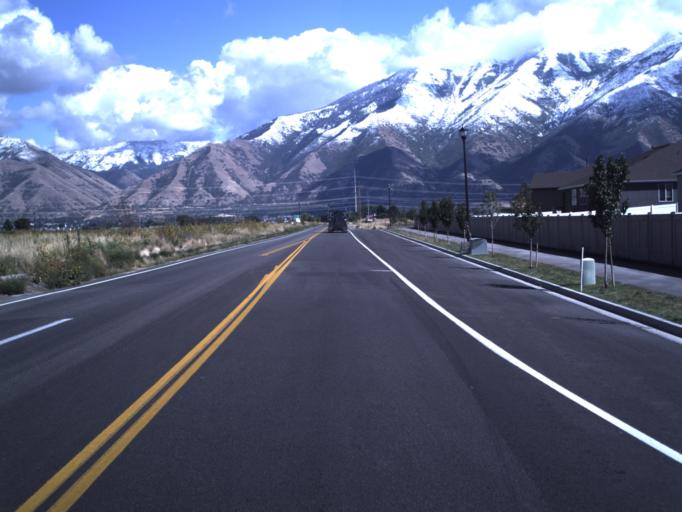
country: US
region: Utah
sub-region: Utah County
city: Spanish Fork
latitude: 40.1154
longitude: -111.6198
